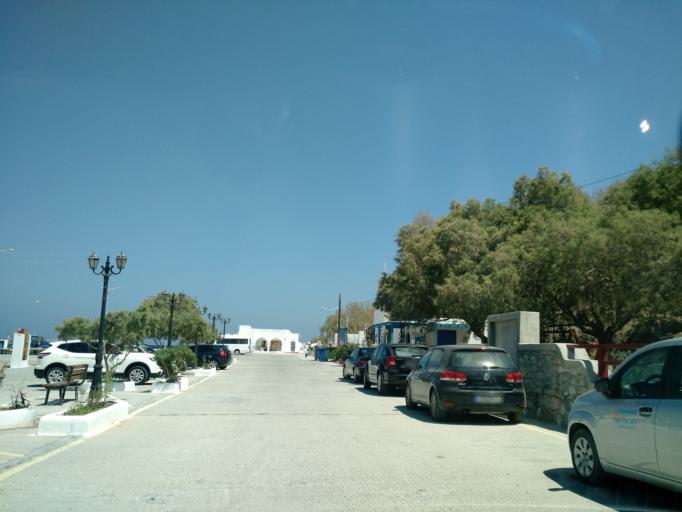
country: GR
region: South Aegean
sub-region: Nomos Dodekanisou
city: Astypalaia
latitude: 36.5473
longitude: 26.3540
